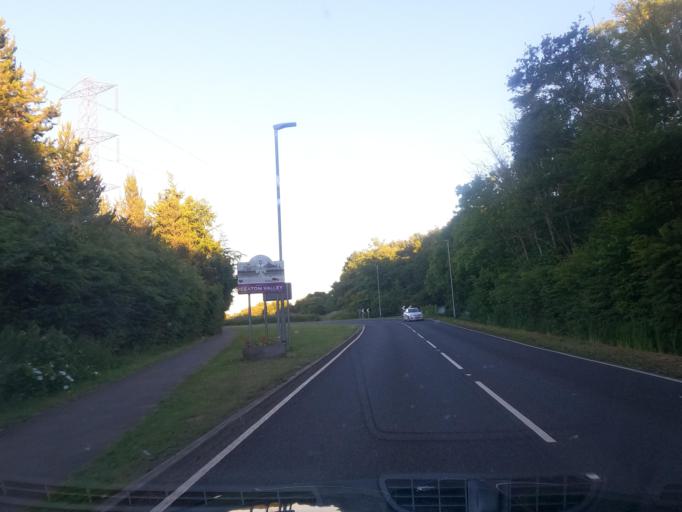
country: GB
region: England
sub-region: Northumberland
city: Seghill
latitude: 55.0774
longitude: -1.5473
